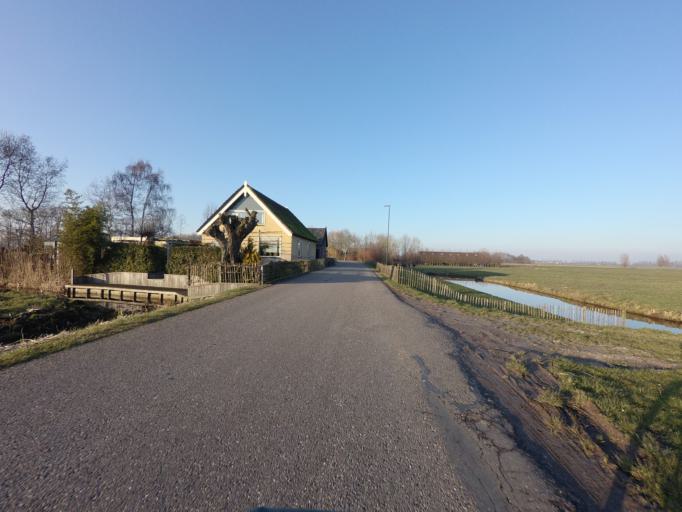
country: NL
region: South Holland
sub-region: Gemeente Giessenlanden
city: Giessenburg
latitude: 51.8916
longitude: 4.9329
